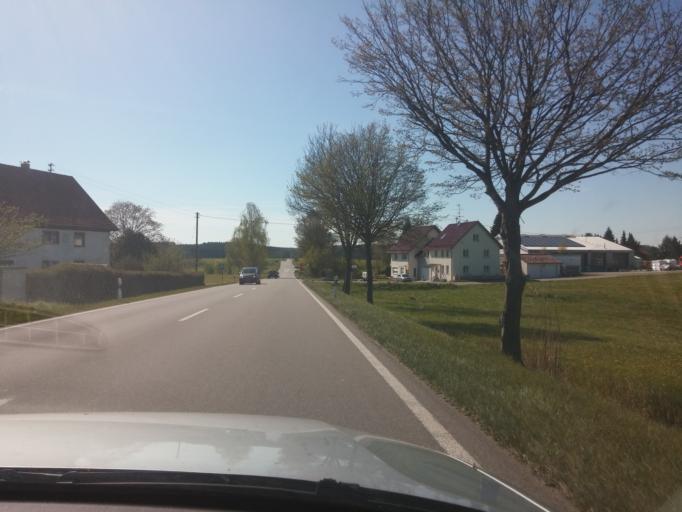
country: DE
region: Baden-Wuerttemberg
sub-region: Tuebingen Region
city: Eberhardzell
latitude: 47.9643
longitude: 9.8194
